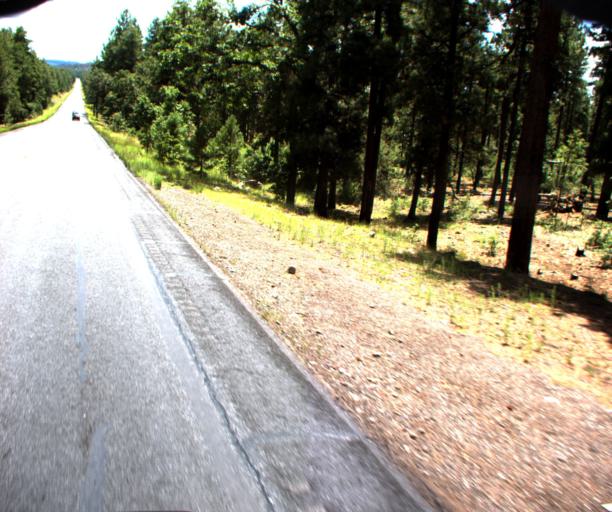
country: US
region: Arizona
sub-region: Gila County
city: Pine
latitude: 34.4849
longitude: -111.4548
